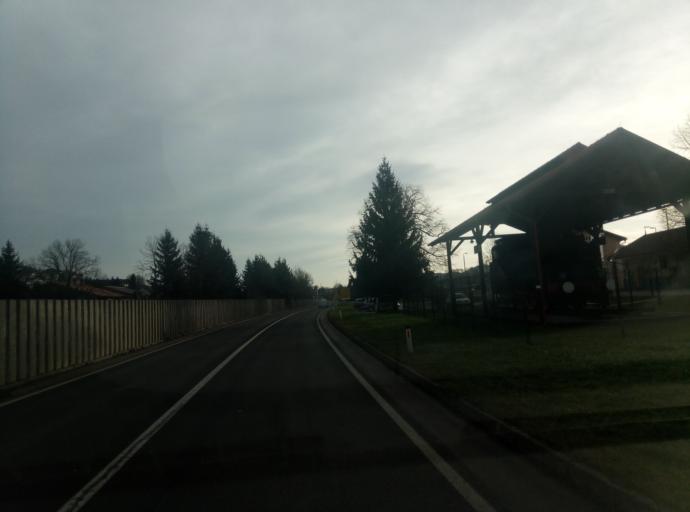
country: SI
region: Sentjur pri Celju
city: Sentjur
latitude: 46.2136
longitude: 15.3952
